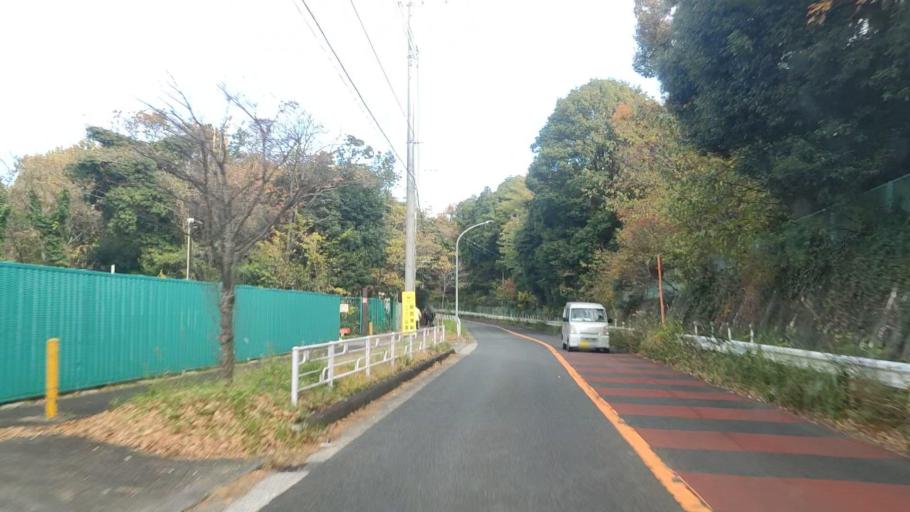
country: JP
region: Kanagawa
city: Minami-rinkan
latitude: 35.4479
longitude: 139.5376
